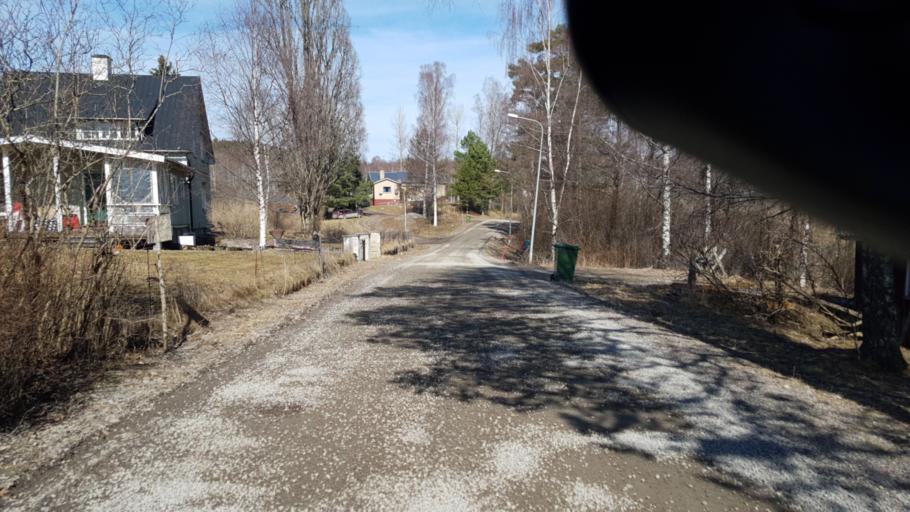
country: SE
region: Vaermland
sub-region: Arvika Kommun
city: Arvika
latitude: 59.5259
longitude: 12.8289
